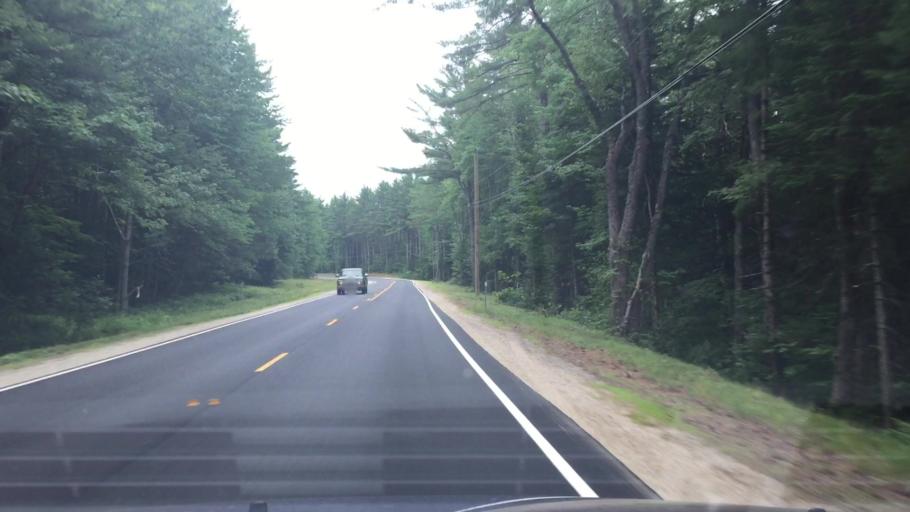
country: US
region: New Hampshire
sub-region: Carroll County
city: Freedom
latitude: 43.8305
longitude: -71.0766
